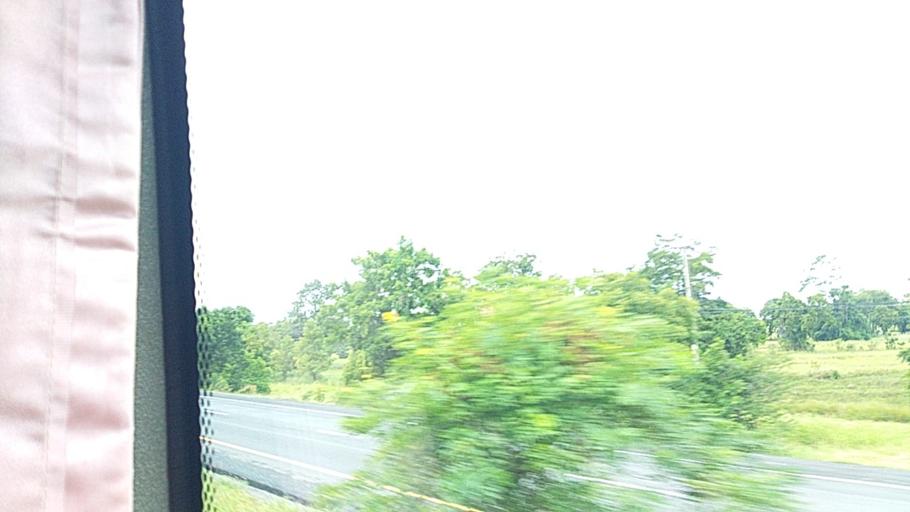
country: TH
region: Nakhon Ratchasima
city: Non Daeng
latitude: 15.4449
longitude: 102.4959
